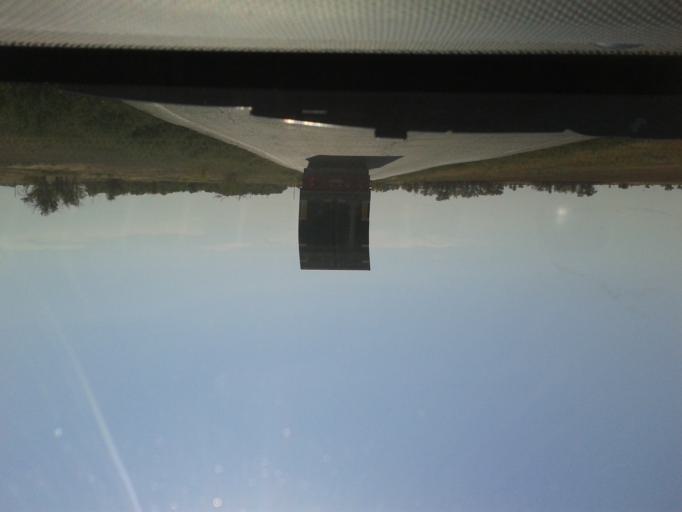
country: RU
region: Astrakhan
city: Znamensk
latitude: 48.6221
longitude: 45.5376
